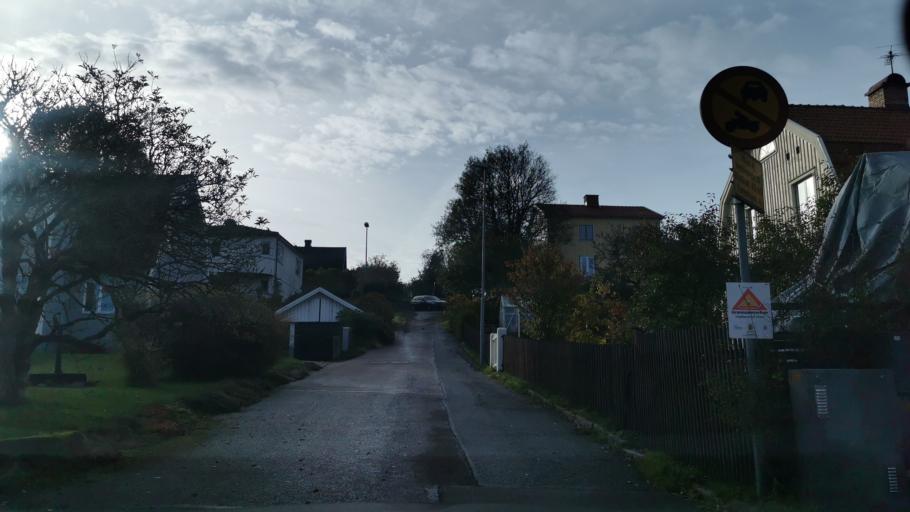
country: SE
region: Vaestra Goetaland
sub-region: Partille Kommun
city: Partille
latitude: 57.7329
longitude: 12.0798
